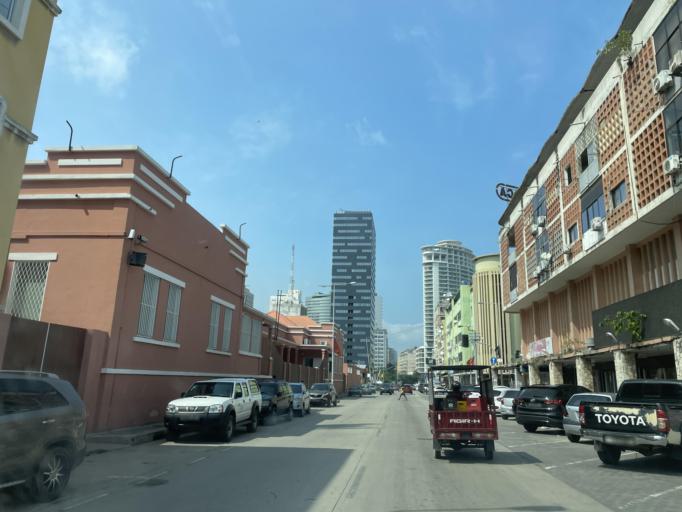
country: AO
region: Luanda
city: Luanda
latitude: -8.8065
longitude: 13.2422
